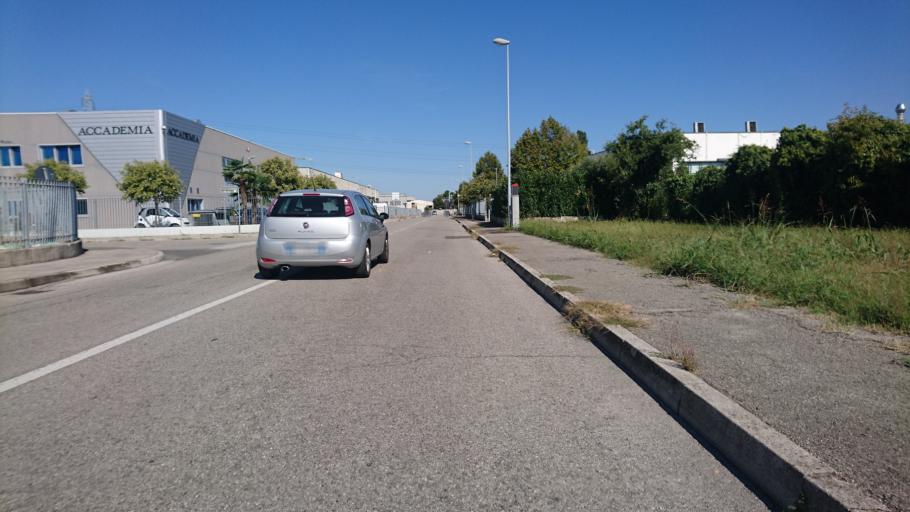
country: IT
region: Veneto
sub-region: Provincia di Venezia
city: Fosso
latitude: 45.3957
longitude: 12.0448
